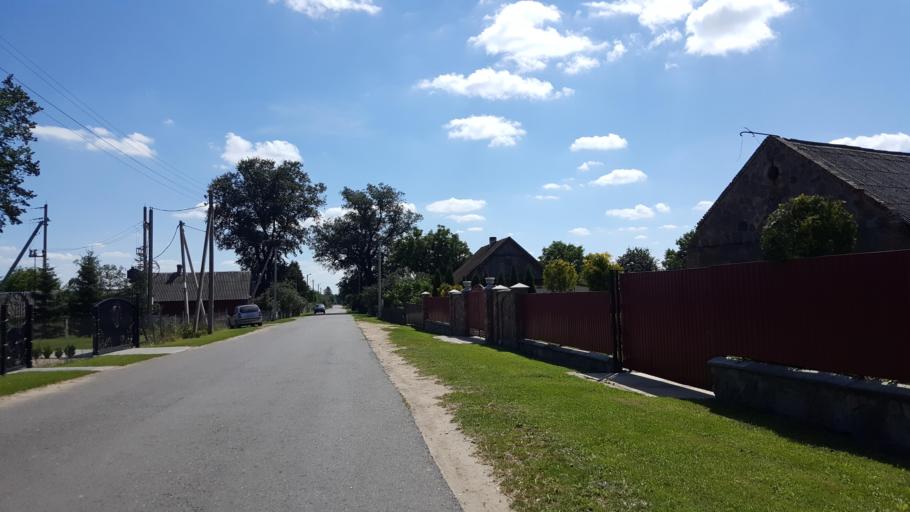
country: BY
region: Brest
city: Charnawchytsy
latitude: 52.3442
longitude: 23.6173
